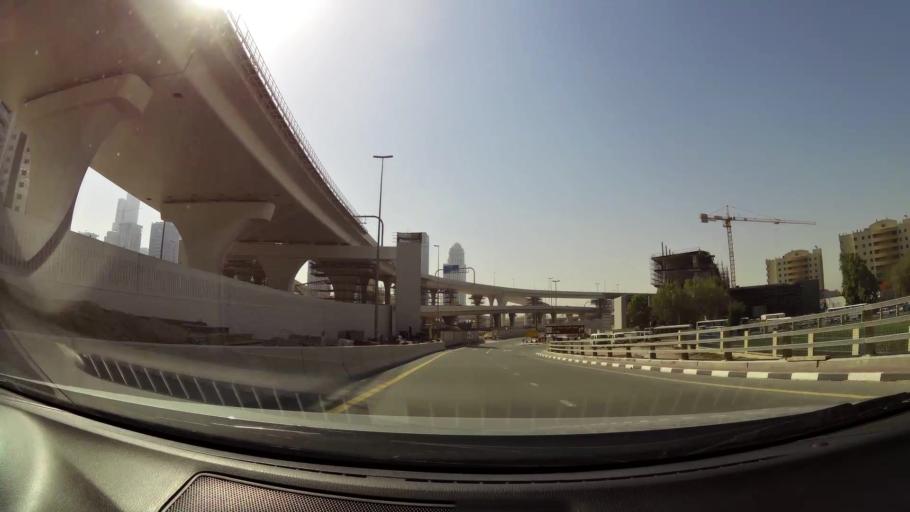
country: AE
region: Dubai
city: Dubai
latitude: 25.0667
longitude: 55.1302
